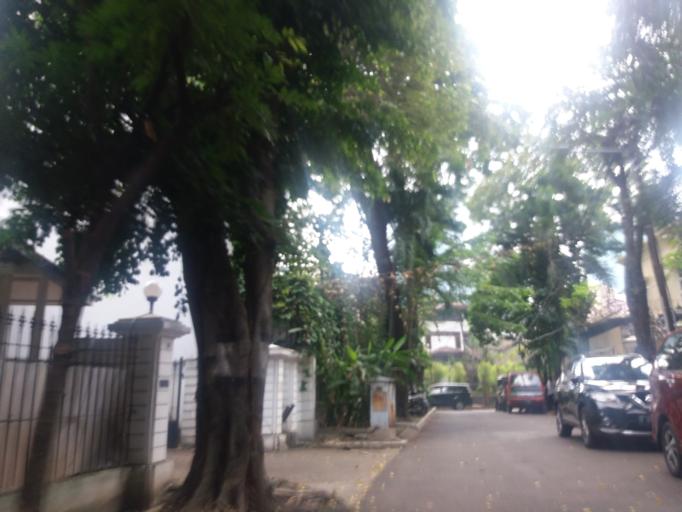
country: ID
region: Jakarta Raya
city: Jakarta
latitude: -6.2306
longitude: 106.8312
